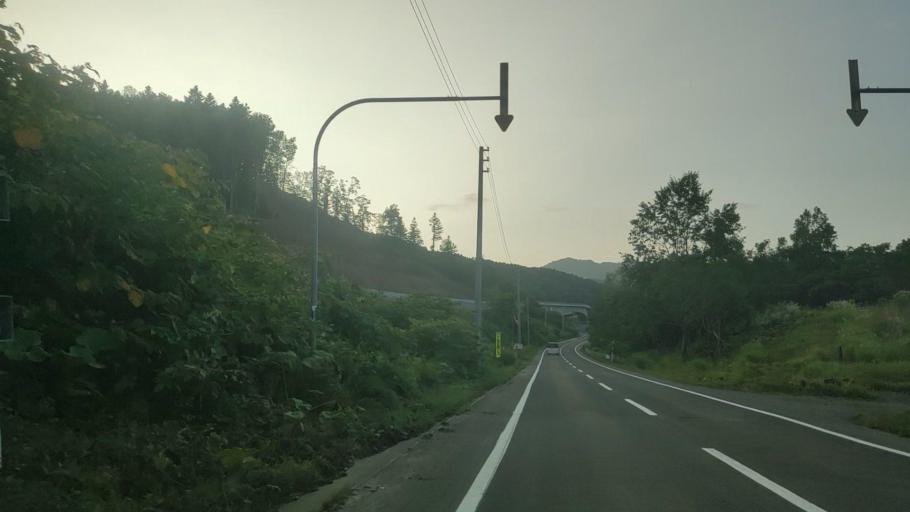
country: JP
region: Hokkaido
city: Bibai
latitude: 43.2247
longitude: 142.0466
